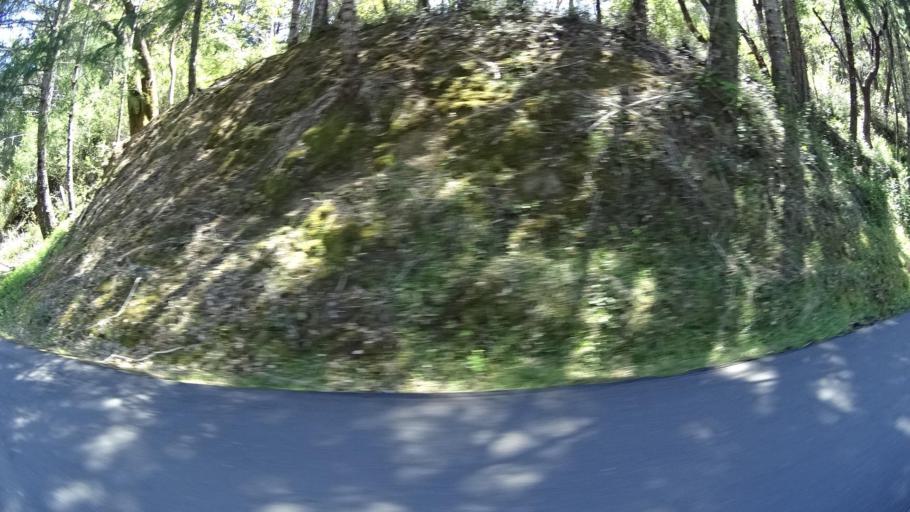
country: US
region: California
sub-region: Humboldt County
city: Rio Dell
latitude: 40.3264
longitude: -124.0482
